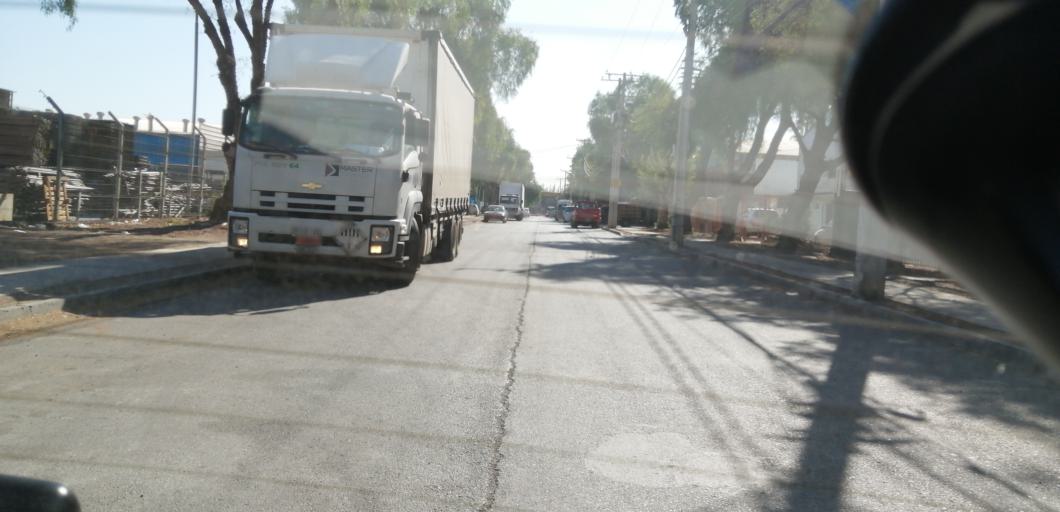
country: CL
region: Santiago Metropolitan
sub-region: Provincia de Santiago
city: Lo Prado
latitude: -33.3832
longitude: -70.7732
